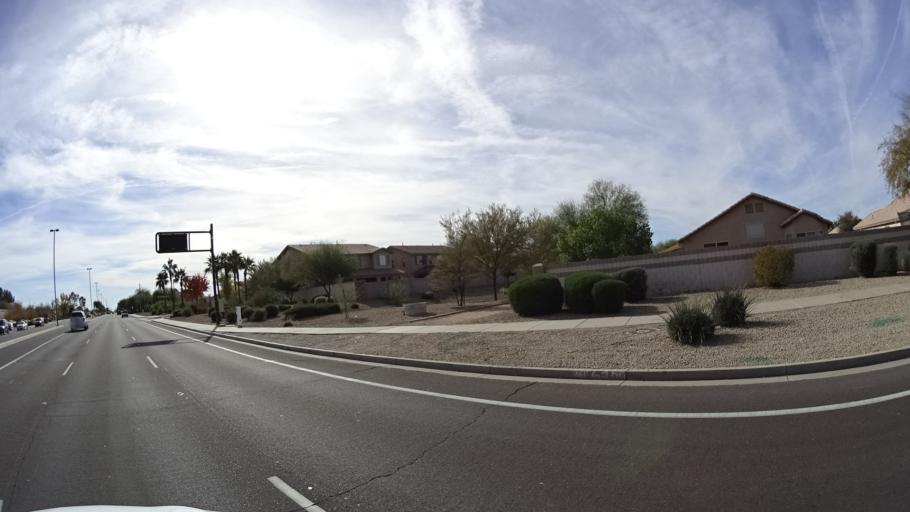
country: US
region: Arizona
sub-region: Maricopa County
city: Gilbert
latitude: 33.3145
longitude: -111.7899
